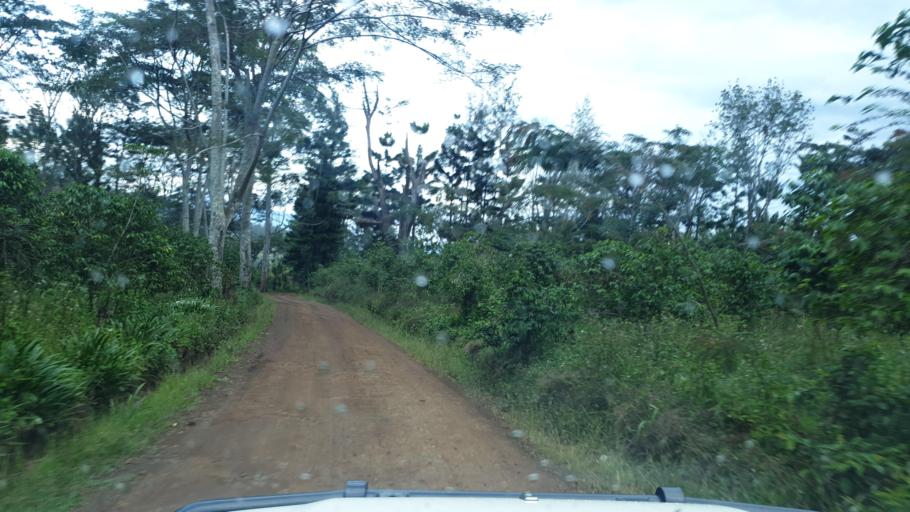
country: PG
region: Eastern Highlands
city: Goroka
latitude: -5.9638
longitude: 145.2734
